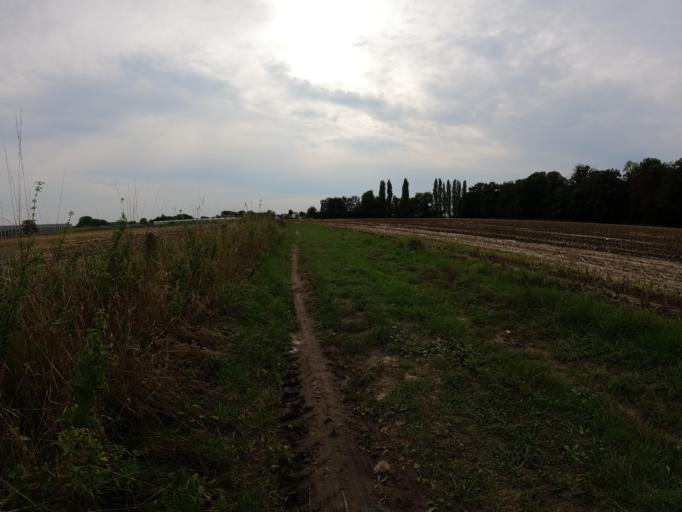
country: BE
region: Flanders
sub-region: Provincie Antwerpen
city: Wommelgem
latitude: 51.1893
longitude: 4.5102
